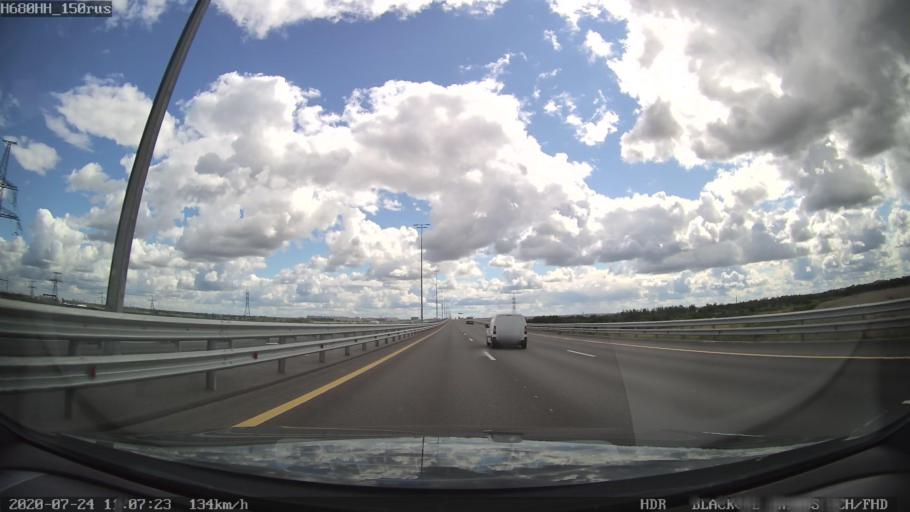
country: RU
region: St.-Petersburg
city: Pushkin
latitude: 59.7563
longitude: 30.4035
